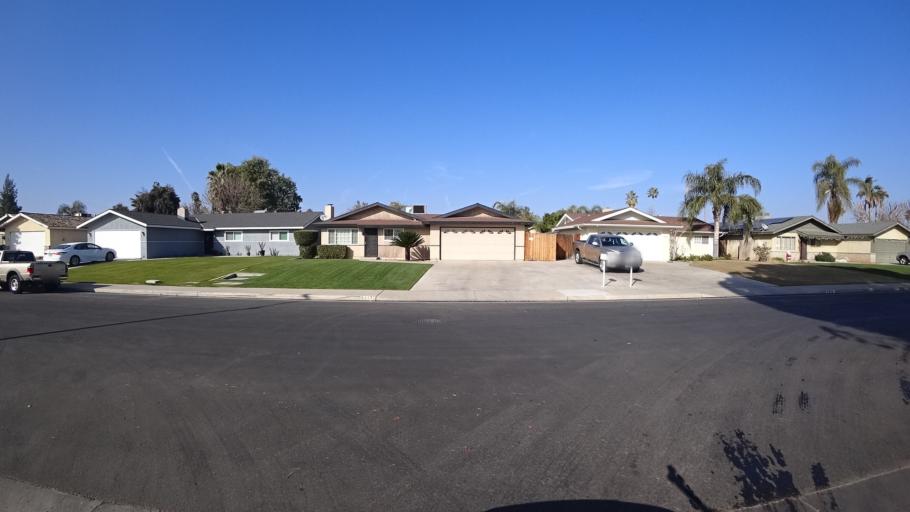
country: US
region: California
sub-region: Kern County
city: Bakersfield
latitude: 35.3303
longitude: -119.0606
